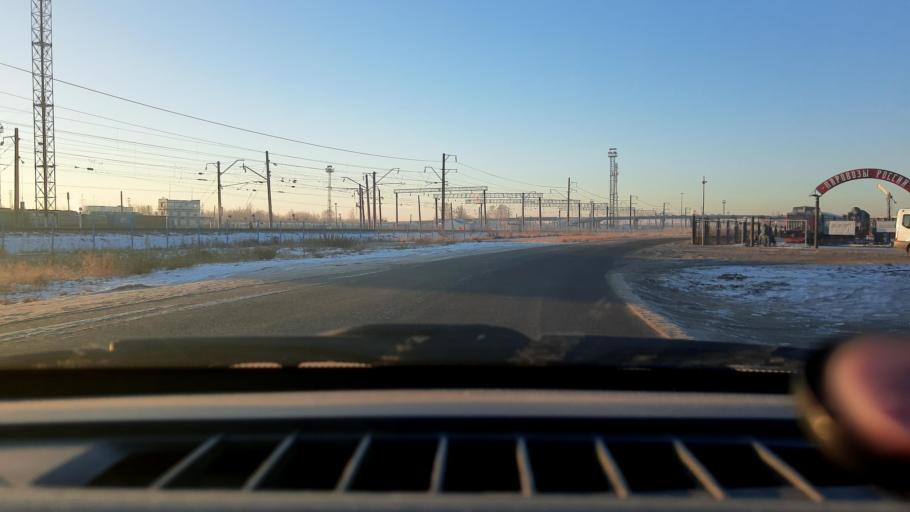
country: RU
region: Nizjnij Novgorod
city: Gorbatovka
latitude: 56.2846
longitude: 43.8475
